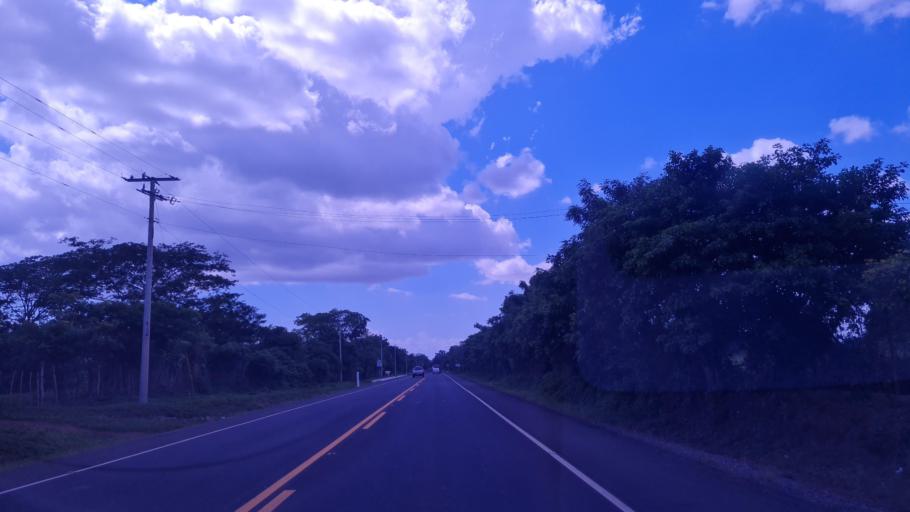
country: NI
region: Masaya
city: Nindiri
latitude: 12.0314
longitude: -86.1242
